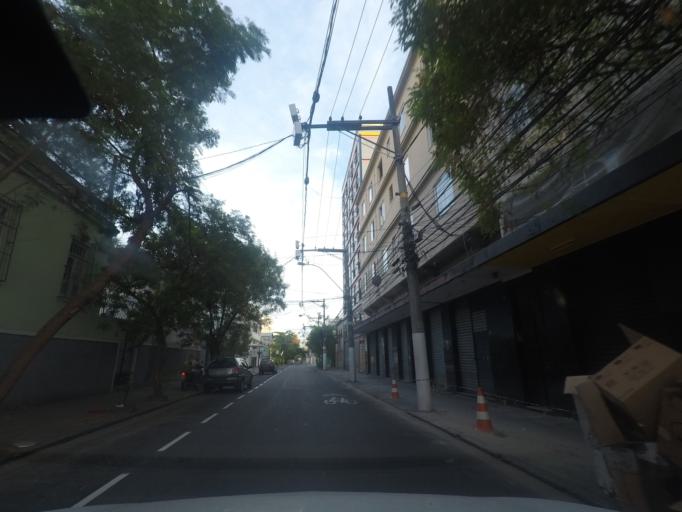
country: BR
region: Rio de Janeiro
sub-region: Niteroi
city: Niteroi
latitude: -22.8895
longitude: -43.1191
